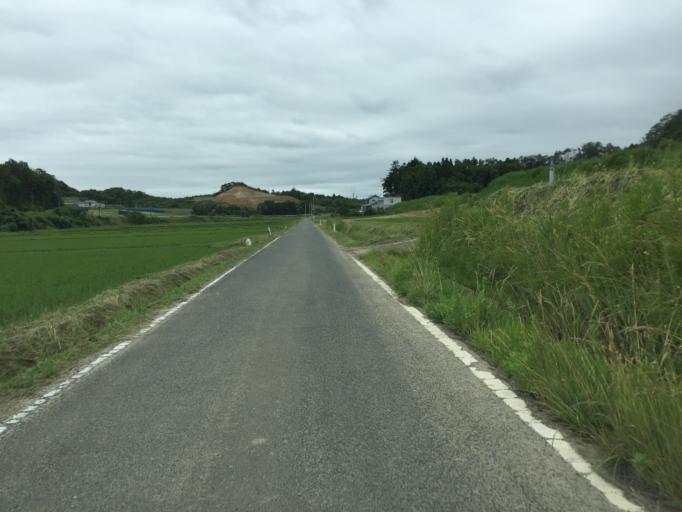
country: JP
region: Fukushima
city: Namie
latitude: 37.7508
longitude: 140.9938
